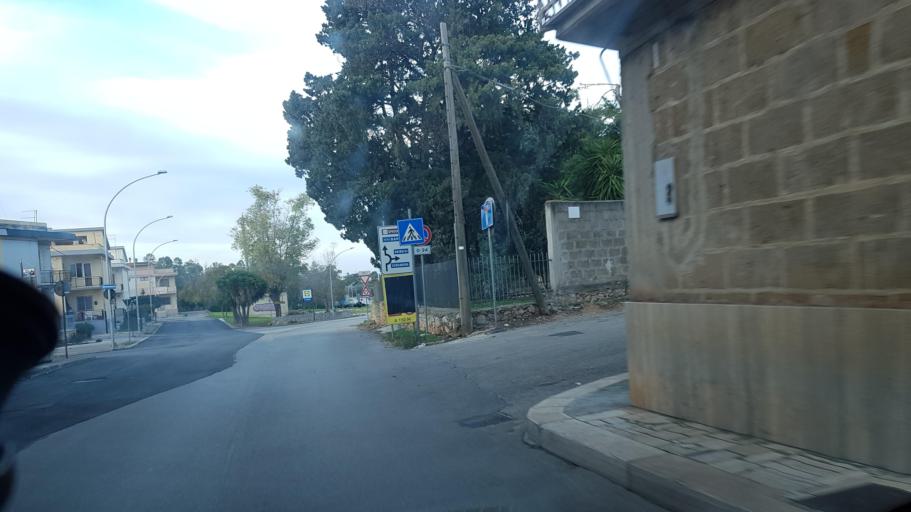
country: IT
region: Apulia
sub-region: Provincia di Brindisi
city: San Vito dei Normanni
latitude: 40.6613
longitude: 17.7053
